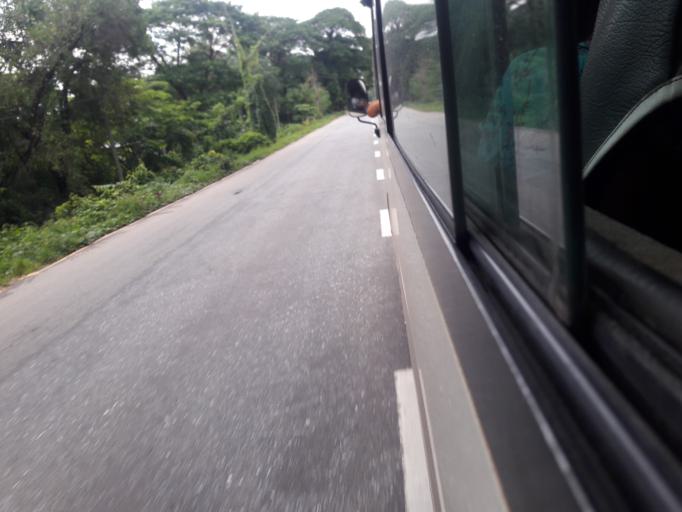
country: MM
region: Bago
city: Nyaunglebin
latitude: 17.8205
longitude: 96.6732
